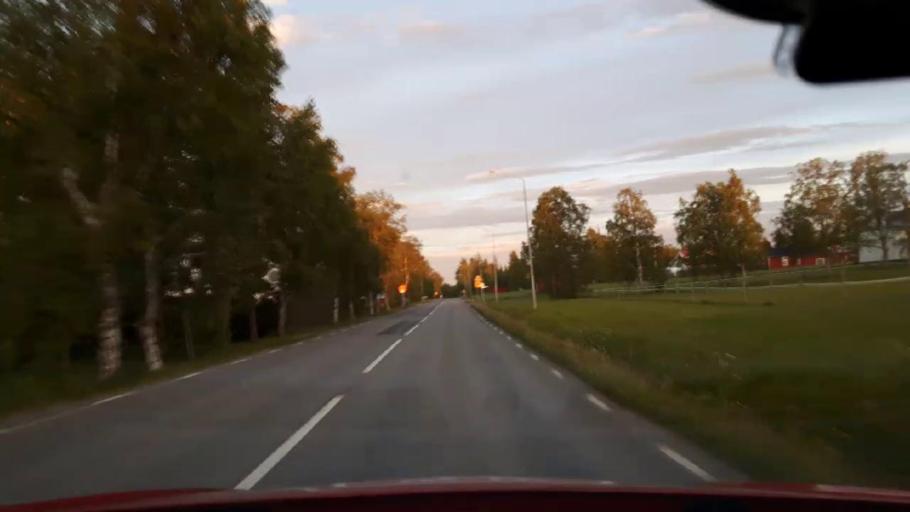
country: SE
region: Jaemtland
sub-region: OEstersunds Kommun
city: Brunflo
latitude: 63.1135
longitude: 14.7292
